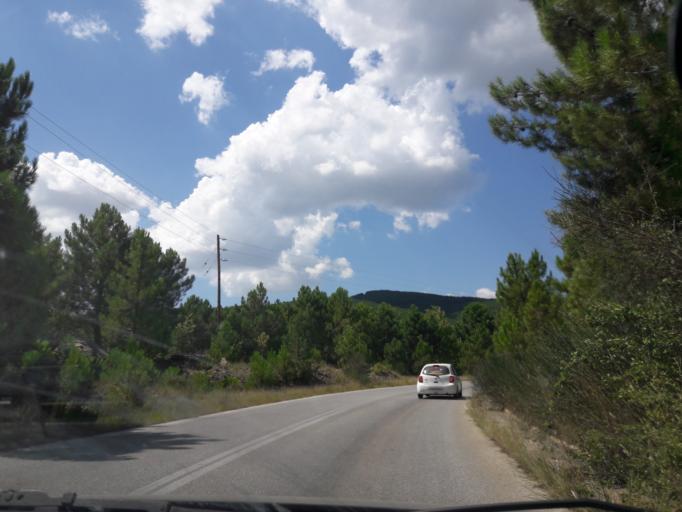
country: GR
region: Central Macedonia
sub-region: Nomos Chalkidikis
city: Polygyros
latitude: 40.3692
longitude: 23.4994
